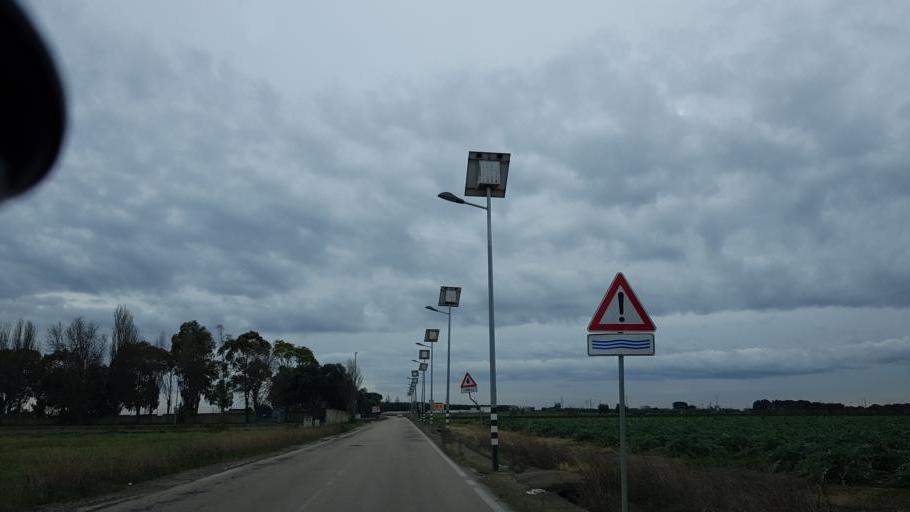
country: IT
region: Apulia
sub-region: Provincia di Brindisi
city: La Rosa
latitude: 40.6154
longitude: 17.9449
